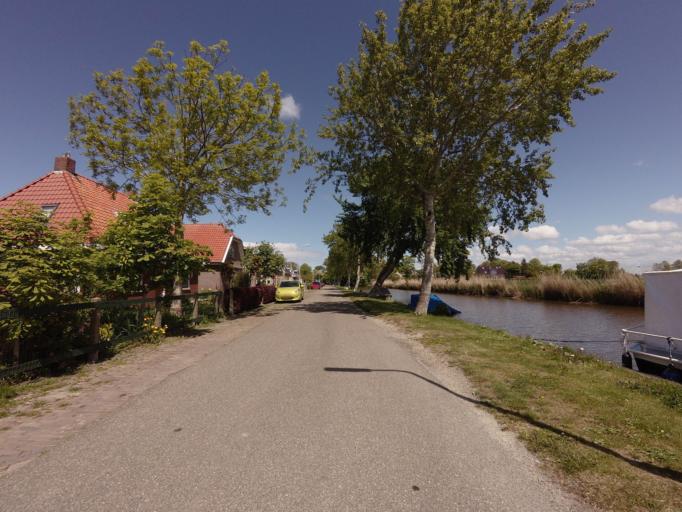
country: NL
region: Friesland
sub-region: Gemeente Harlingen
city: Harlingen
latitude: 53.1396
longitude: 5.4368
